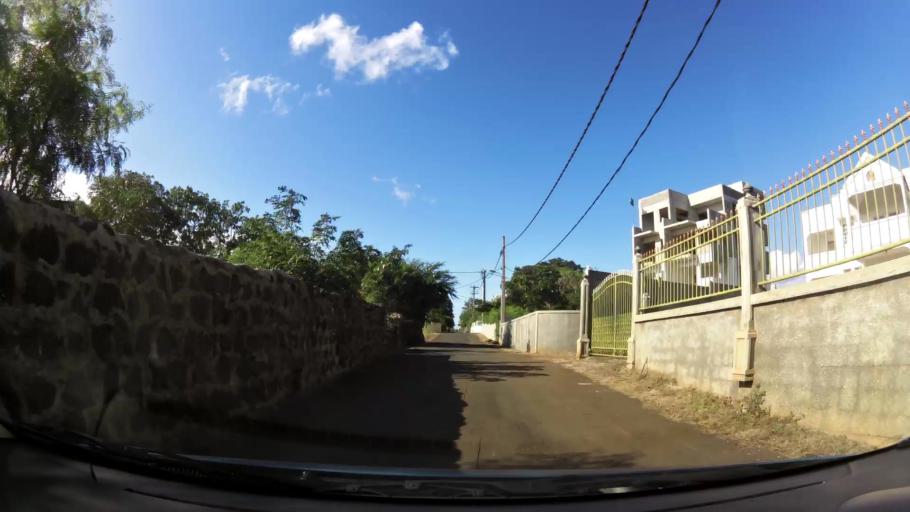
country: MU
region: Black River
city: Albion
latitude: -20.1982
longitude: 57.4078
